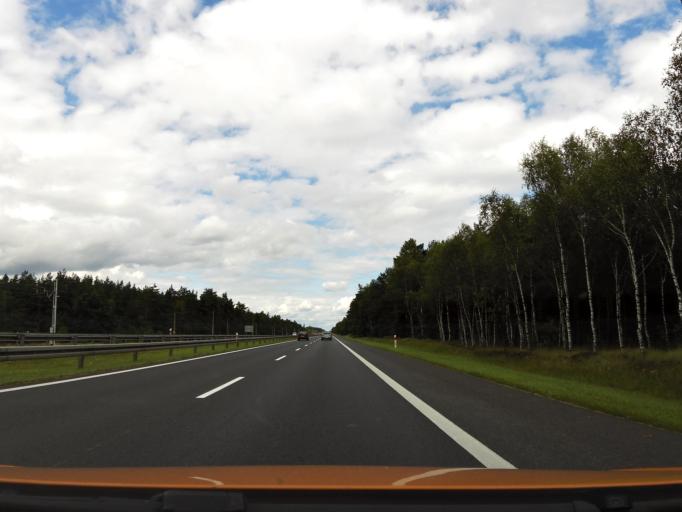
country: PL
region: West Pomeranian Voivodeship
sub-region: Powiat goleniowski
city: Goleniow
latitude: 53.4814
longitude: 14.7920
